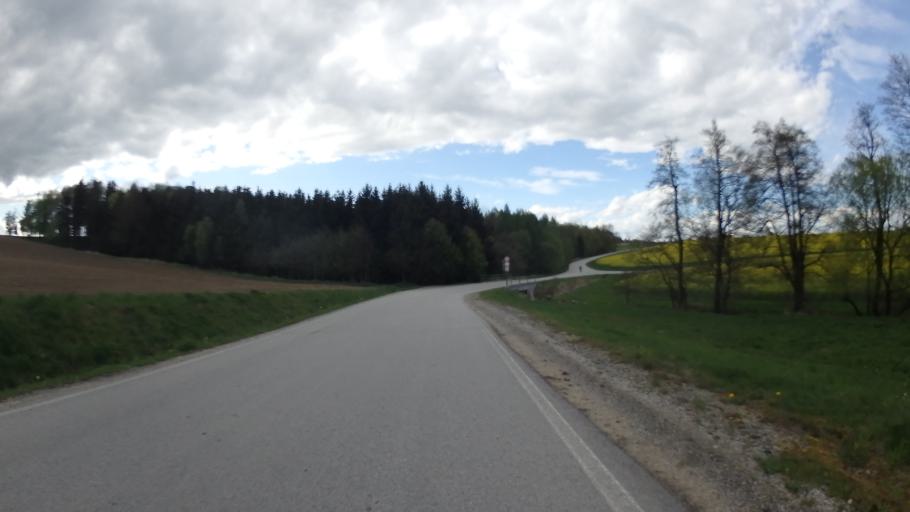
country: CZ
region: Vysocina
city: Merin
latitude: 49.3727
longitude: 15.8934
